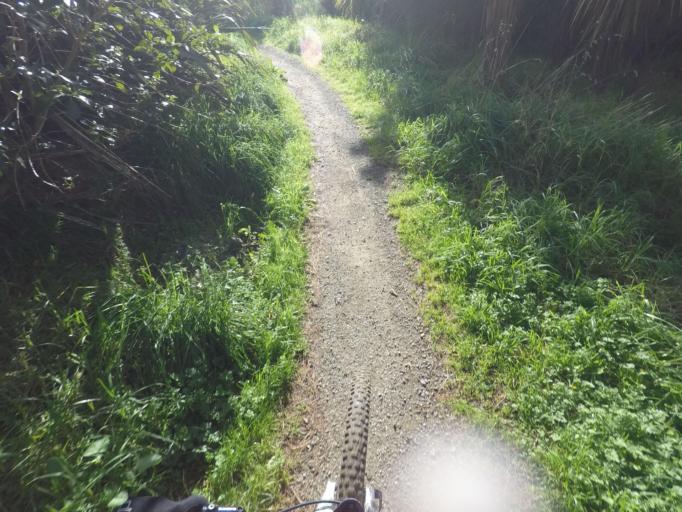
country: NZ
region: Auckland
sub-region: Auckland
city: Manukau City
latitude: -36.9991
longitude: 174.9108
